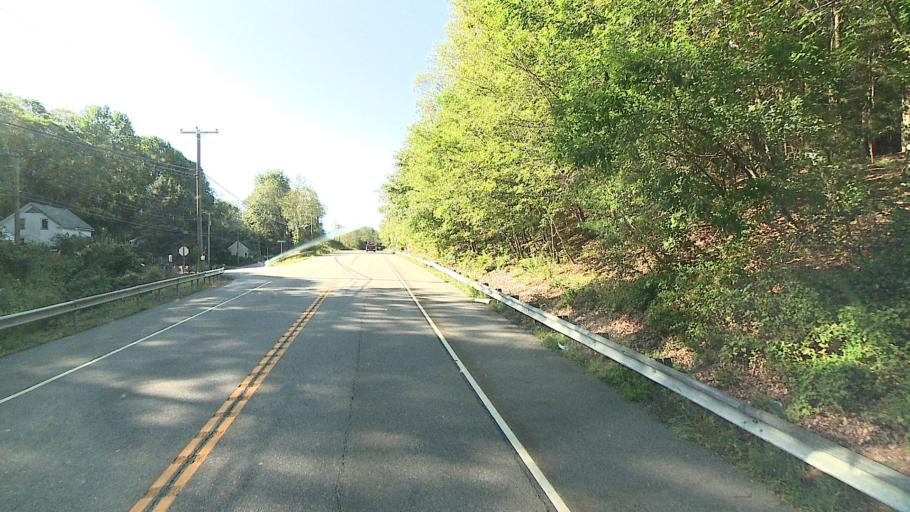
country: US
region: Connecticut
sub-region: New London County
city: Gales Ferry
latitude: 41.4380
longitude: -72.0800
